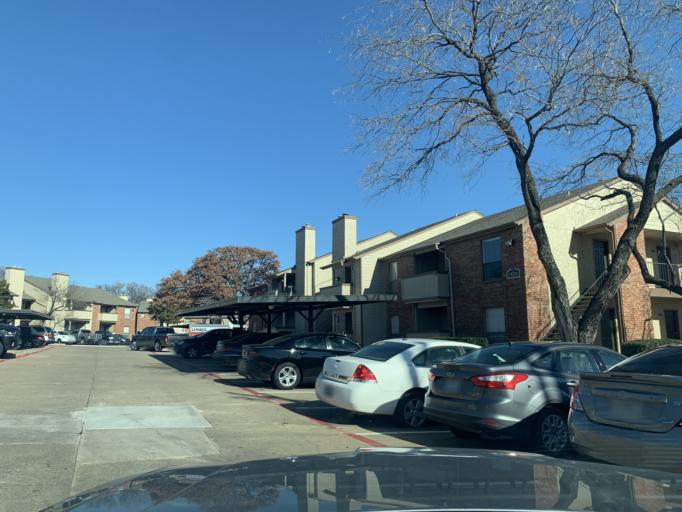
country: US
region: Texas
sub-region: Tarrant County
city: Bedford
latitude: 32.8399
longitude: -97.1465
